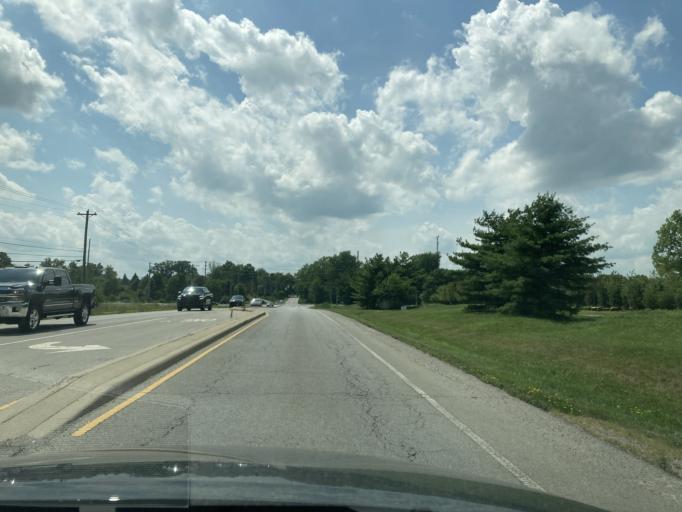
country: US
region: Indiana
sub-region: Boone County
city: Zionsville
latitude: 39.9985
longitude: -86.2622
